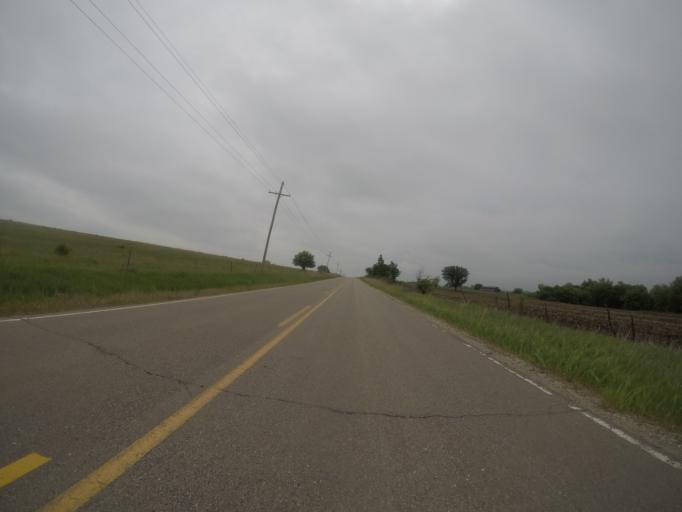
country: US
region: Kansas
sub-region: Pottawatomie County
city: Westmoreland
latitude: 39.5222
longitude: -96.2617
